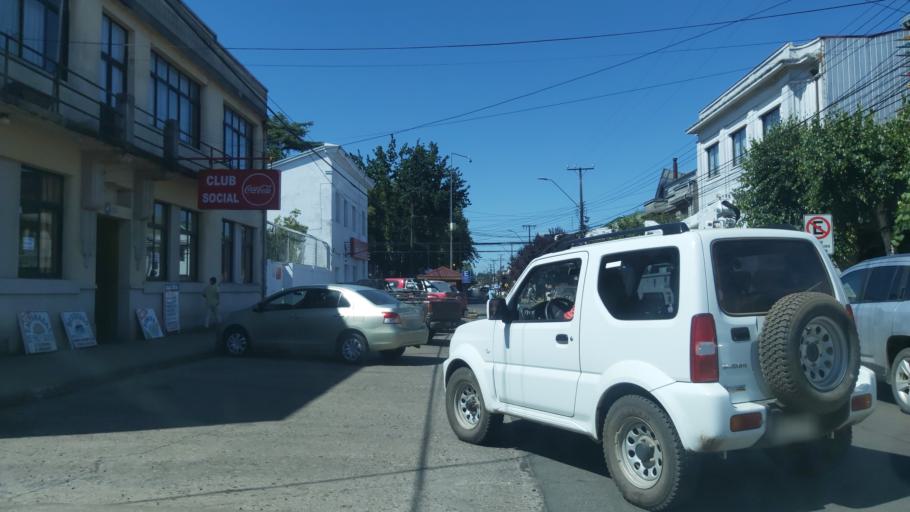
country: CL
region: Araucania
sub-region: Provincia de Malleco
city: Victoria
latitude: -38.2330
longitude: -72.3322
